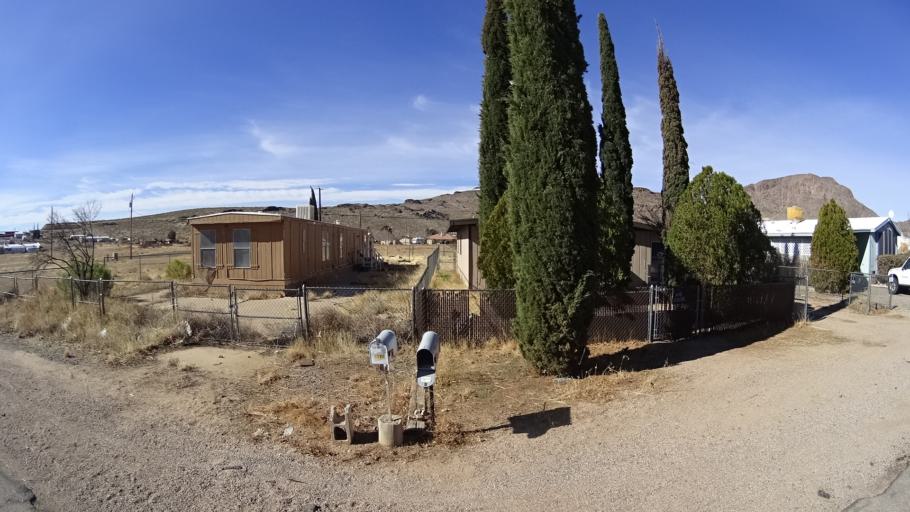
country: US
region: Arizona
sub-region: Mohave County
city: New Kingman-Butler
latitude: 35.2609
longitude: -114.0376
